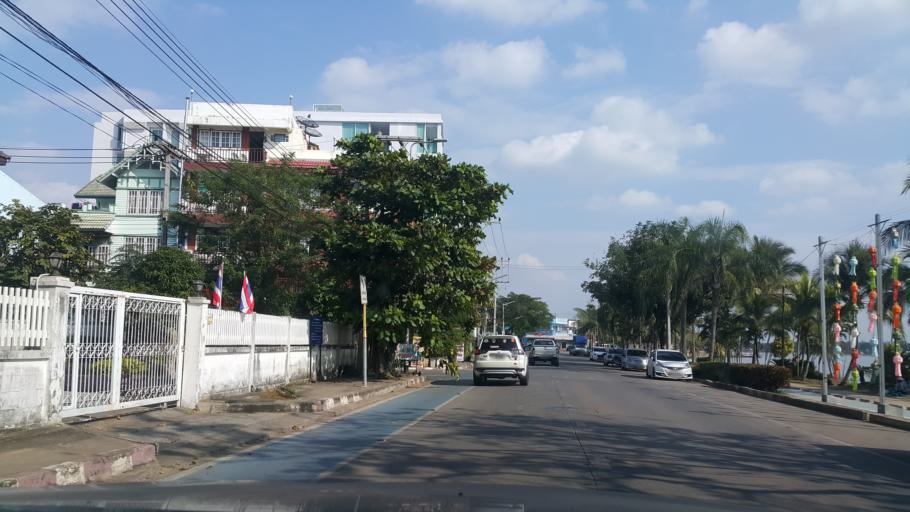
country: TH
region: Phayao
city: Phayao
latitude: 19.1640
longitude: 99.8975
